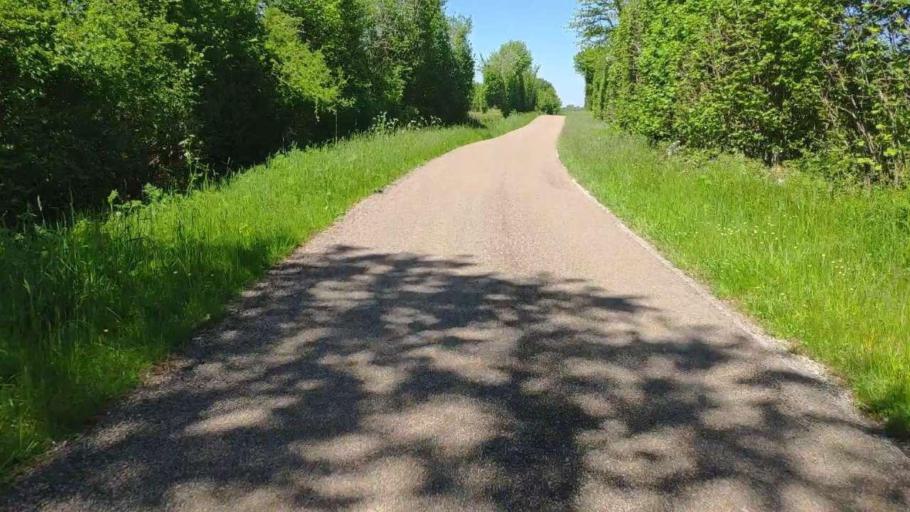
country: FR
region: Franche-Comte
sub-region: Departement du Jura
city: Poligny
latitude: 46.7342
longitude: 5.7221
